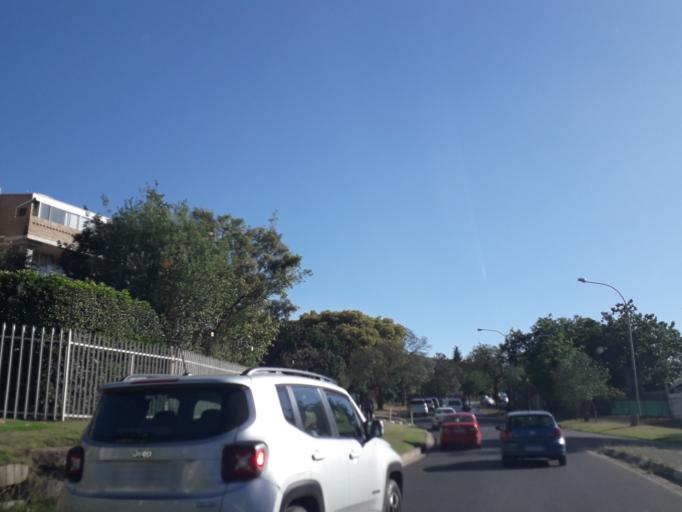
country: ZA
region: Gauteng
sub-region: City of Johannesburg Metropolitan Municipality
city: Roodepoort
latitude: -26.1312
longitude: 27.9676
